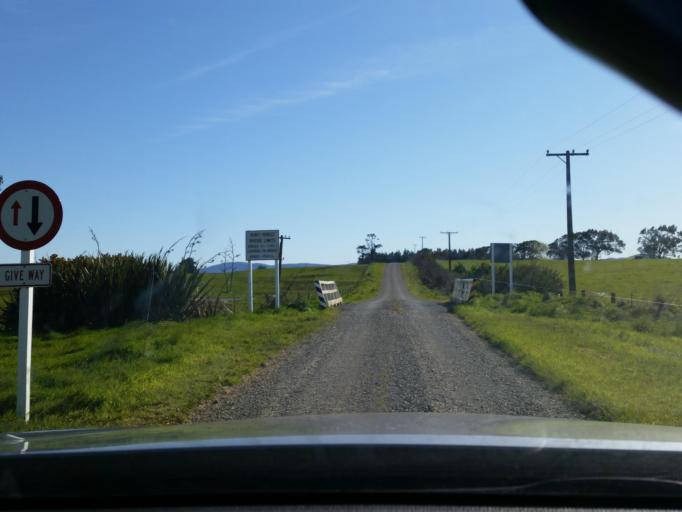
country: NZ
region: Southland
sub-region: Southland District
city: Winton
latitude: -46.2165
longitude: 168.4808
